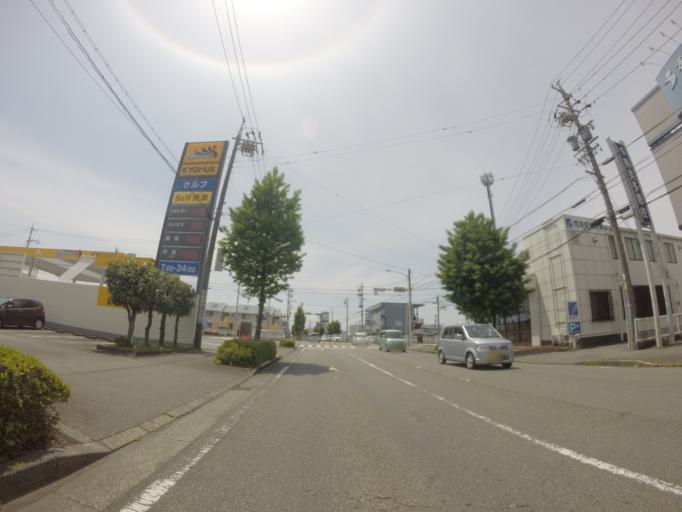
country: JP
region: Shizuoka
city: Yaizu
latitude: 34.8532
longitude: 138.3088
